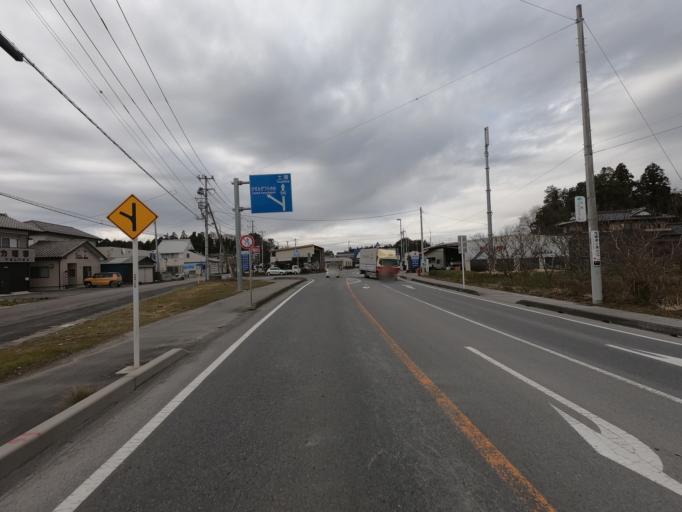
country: JP
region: Ibaraki
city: Ishioka
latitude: 36.0908
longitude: 140.3048
